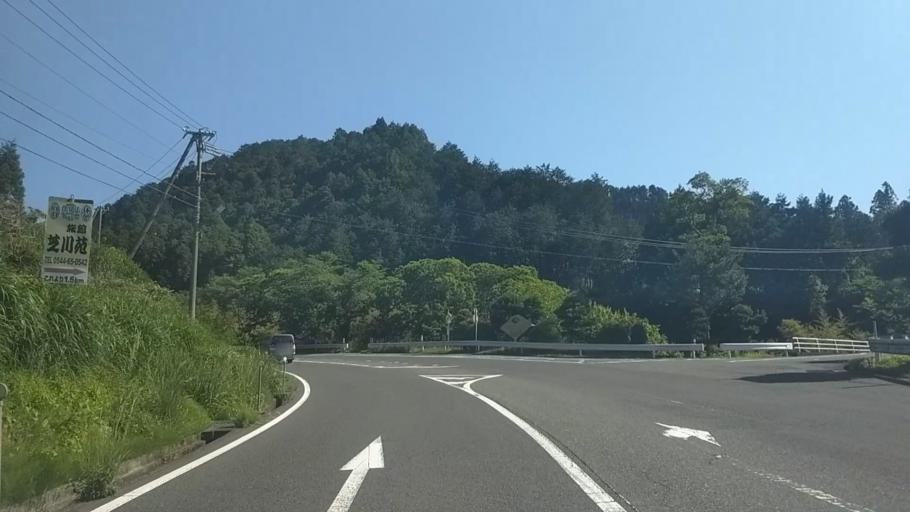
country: JP
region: Shizuoka
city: Fujinomiya
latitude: 35.1712
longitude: 138.5238
